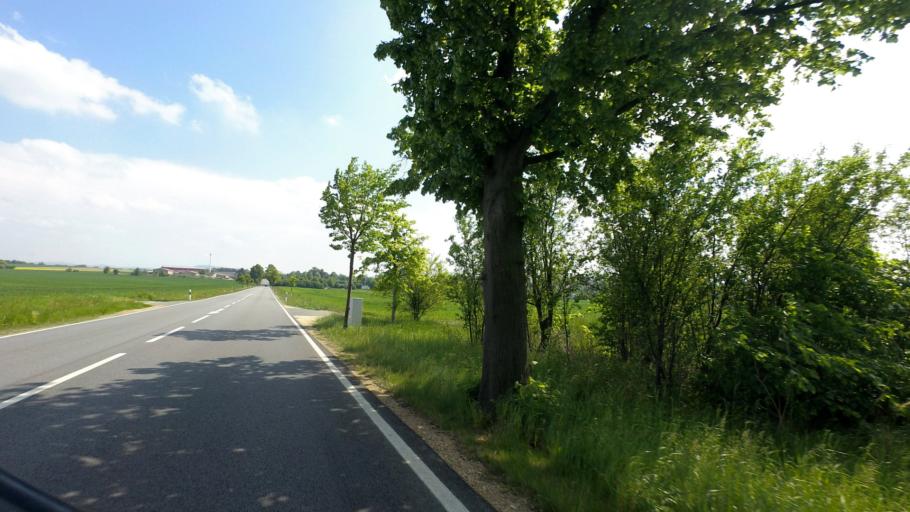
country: DE
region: Saxony
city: Weissenberg
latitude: 51.2021
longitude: 14.6655
